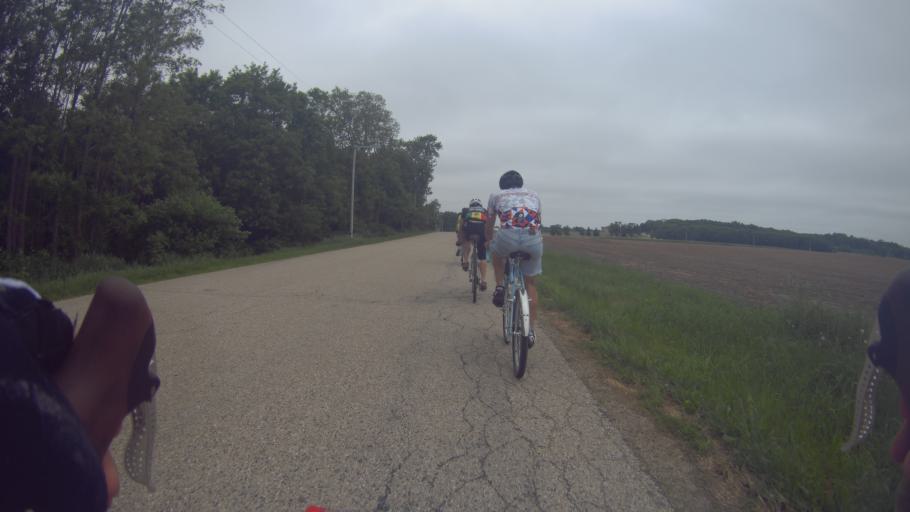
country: US
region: Wisconsin
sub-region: Green County
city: Brooklyn
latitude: 42.8749
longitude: -89.3959
